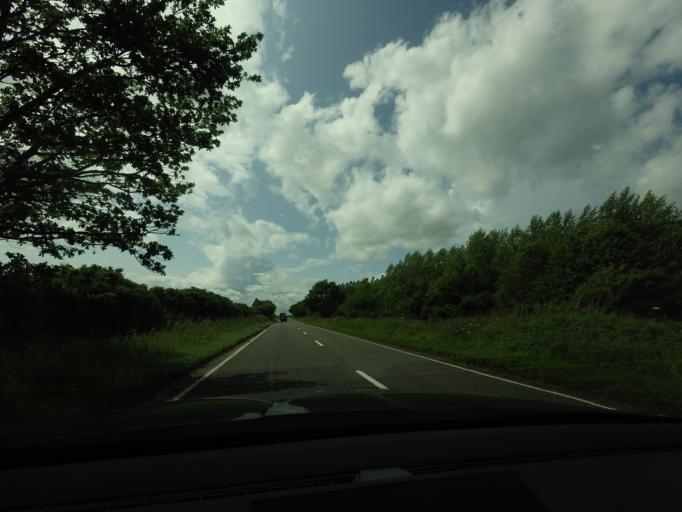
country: GB
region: Scotland
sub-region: Highland
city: Nairn
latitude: 57.5848
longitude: -3.7506
